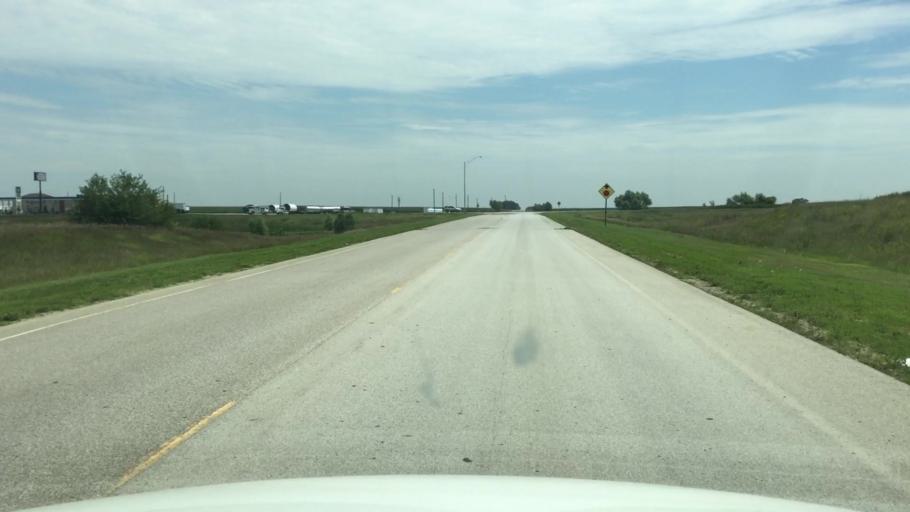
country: US
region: Kansas
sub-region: Nemaha County
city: Sabetha
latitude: 39.8852
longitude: -95.7843
